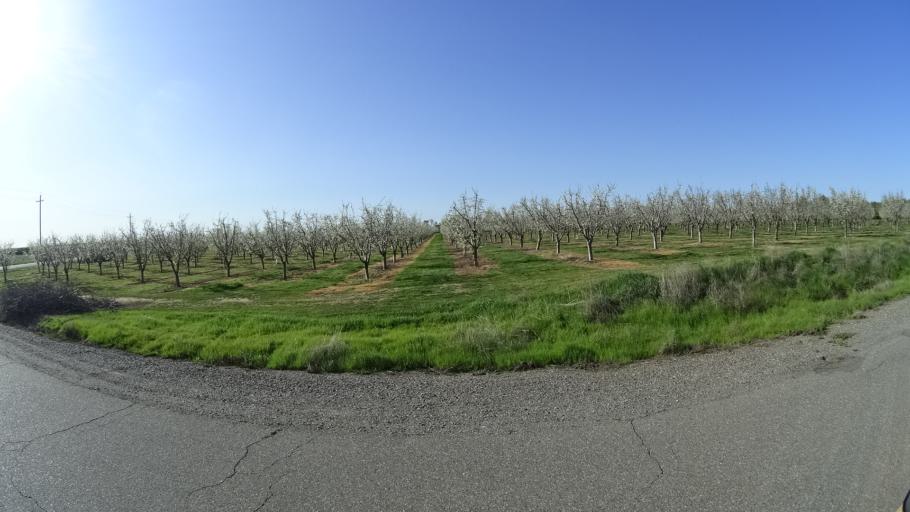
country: US
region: California
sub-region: Glenn County
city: Hamilton City
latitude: 39.7574
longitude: -122.1044
